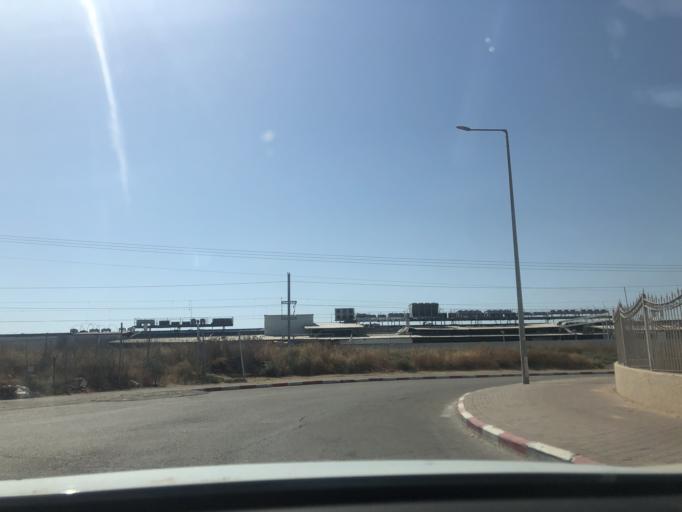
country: IL
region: Central District
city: Lod
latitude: 31.9634
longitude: 34.8989
